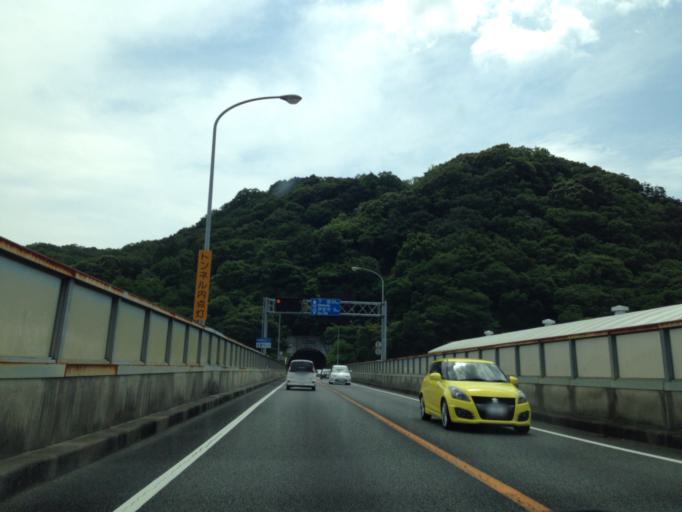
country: JP
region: Shizuoka
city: Mishima
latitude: 35.0259
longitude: 138.9288
